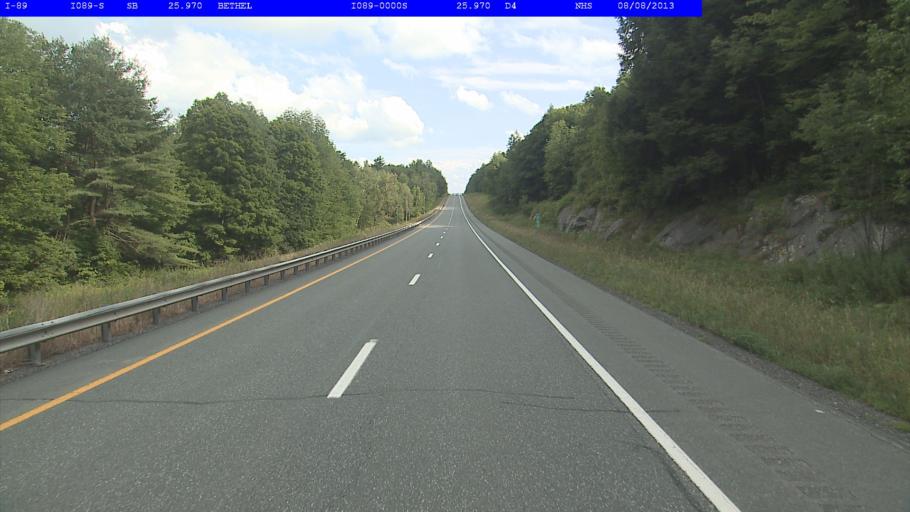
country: US
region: Vermont
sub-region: Orange County
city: Randolph
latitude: 43.8754
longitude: -72.6144
